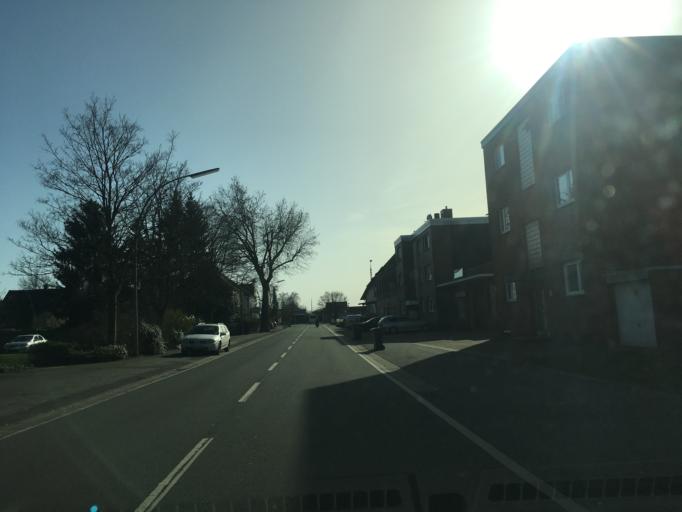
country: DE
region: North Rhine-Westphalia
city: Selm
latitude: 51.7082
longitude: 7.4547
